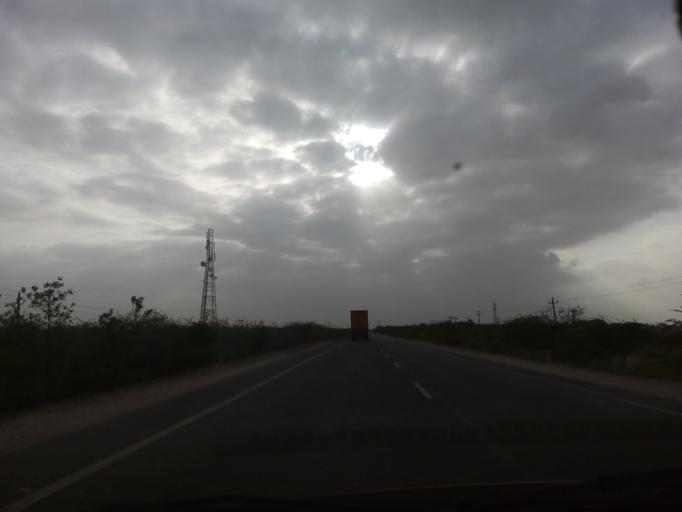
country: IN
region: Gujarat
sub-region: Kachchh
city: Bhuj
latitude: 23.2429
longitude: 69.8176
